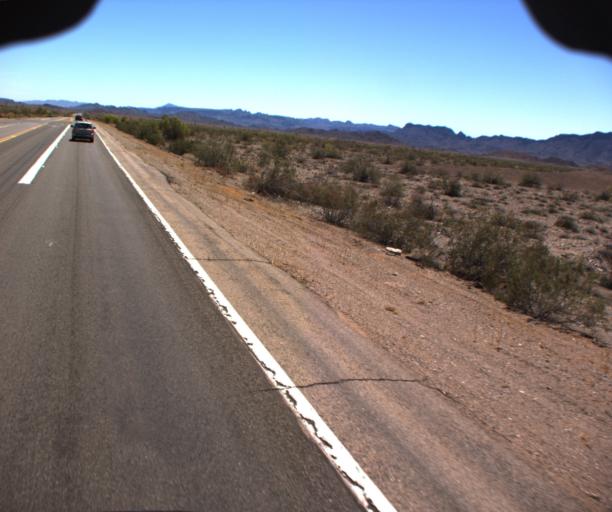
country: US
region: Arizona
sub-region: Mohave County
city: Lake Havasu City
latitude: 34.4168
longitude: -114.1968
